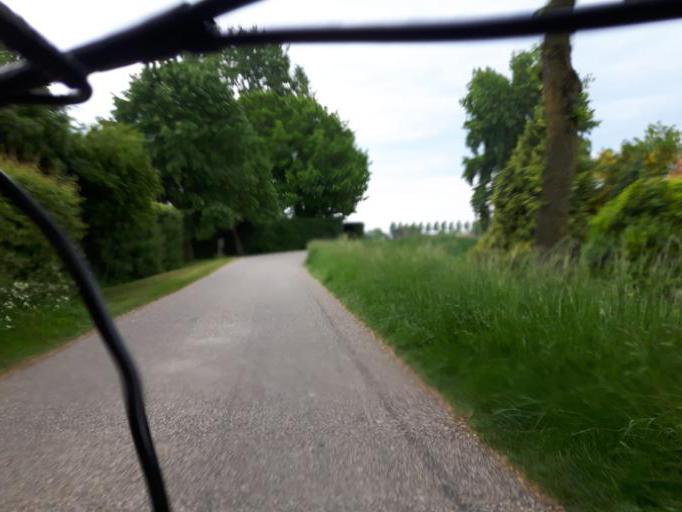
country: NL
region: Zeeland
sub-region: Gemeente Goes
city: Goes
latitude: 51.4384
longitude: 3.8336
